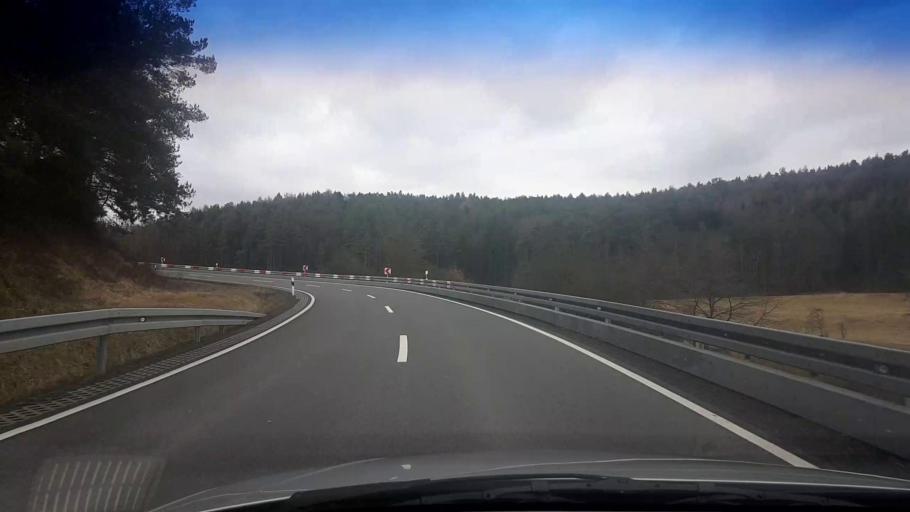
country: DE
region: Bavaria
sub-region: Regierungsbezirk Unterfranken
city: Eltmann
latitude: 49.9351
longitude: 10.6431
